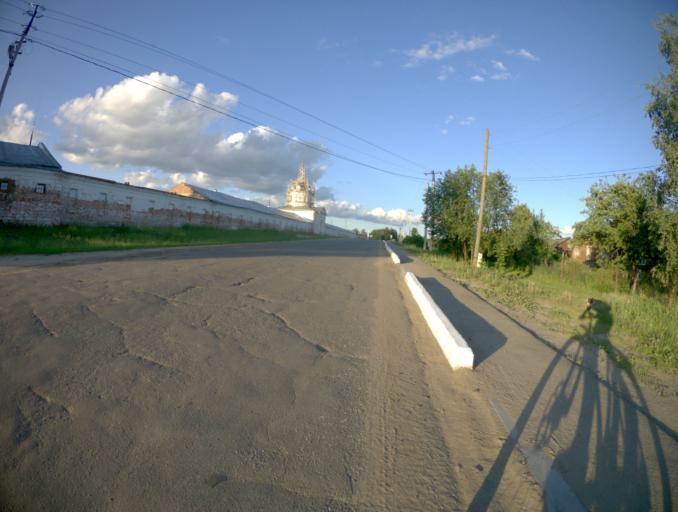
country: RU
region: Ivanovo
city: Gavrilov Posad
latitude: 56.5591
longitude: 40.1333
